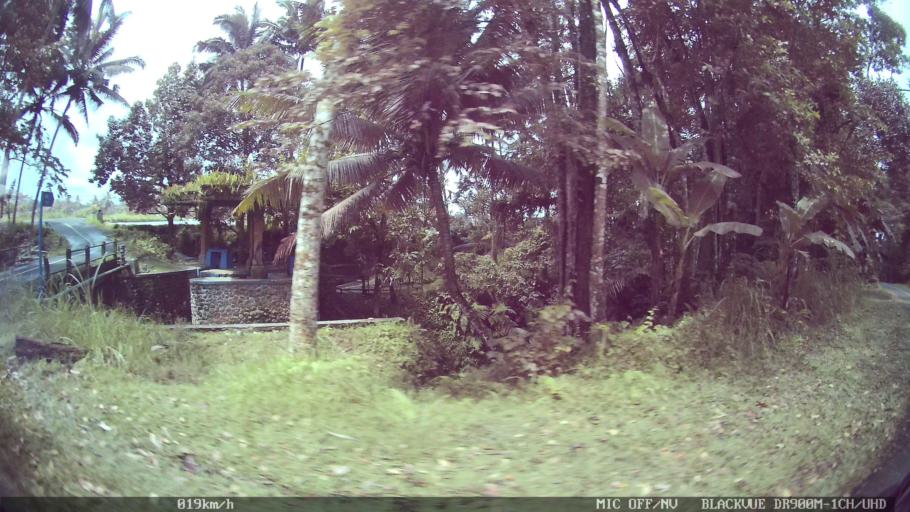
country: ID
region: Bali
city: Bunutan
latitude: -8.4608
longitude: 115.2333
